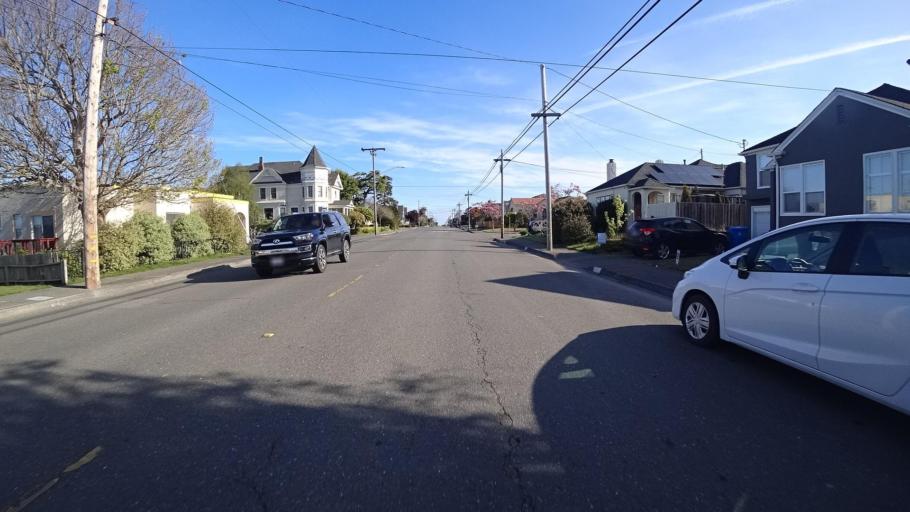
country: US
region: California
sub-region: Humboldt County
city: Eureka
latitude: 40.7849
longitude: -124.1646
